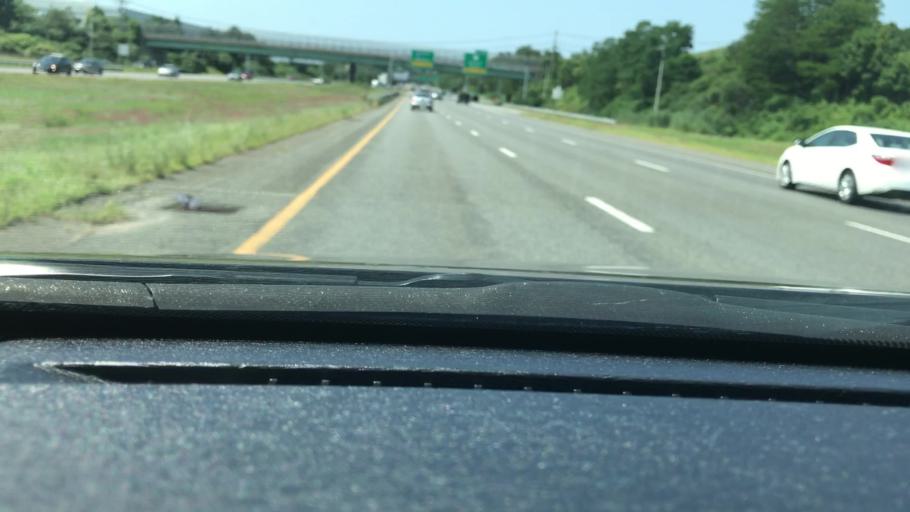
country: US
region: Massachusetts
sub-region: Essex County
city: South Peabody
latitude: 42.5242
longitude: -70.9793
